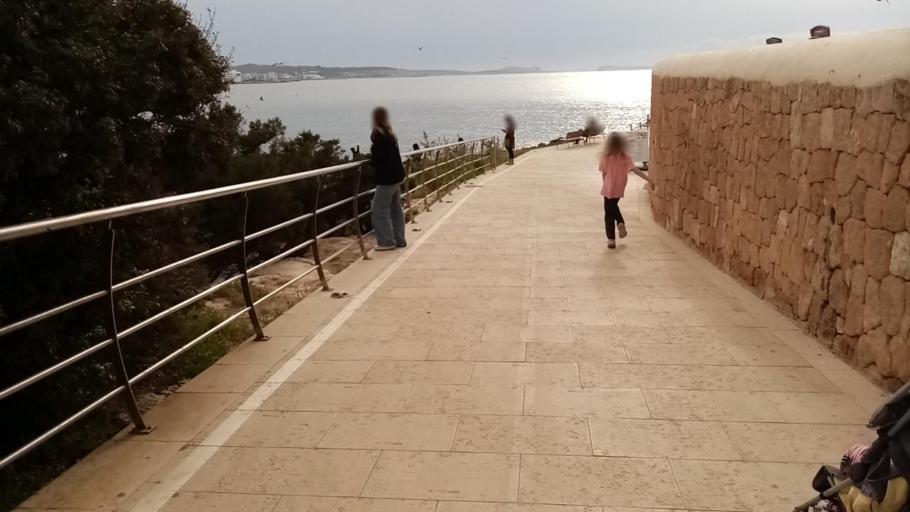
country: ES
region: Balearic Islands
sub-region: Illes Balears
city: Sant Antoni de Portmany
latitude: 38.9796
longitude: 1.2975
